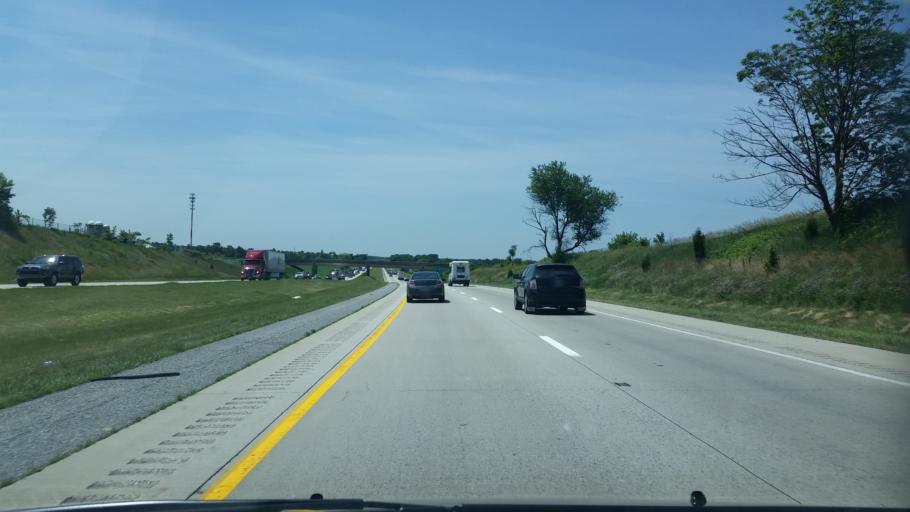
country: US
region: Pennsylvania
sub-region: Franklin County
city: Scotland
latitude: 39.9835
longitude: -77.5680
